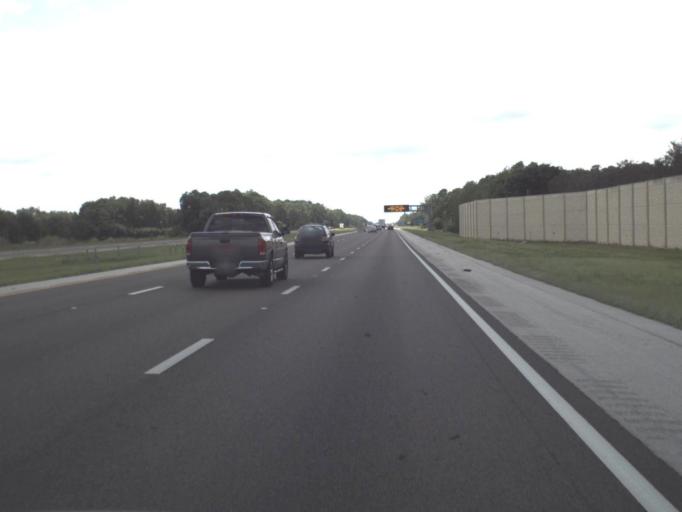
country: US
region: Florida
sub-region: Collier County
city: Vineyards
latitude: 26.2394
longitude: -81.7369
